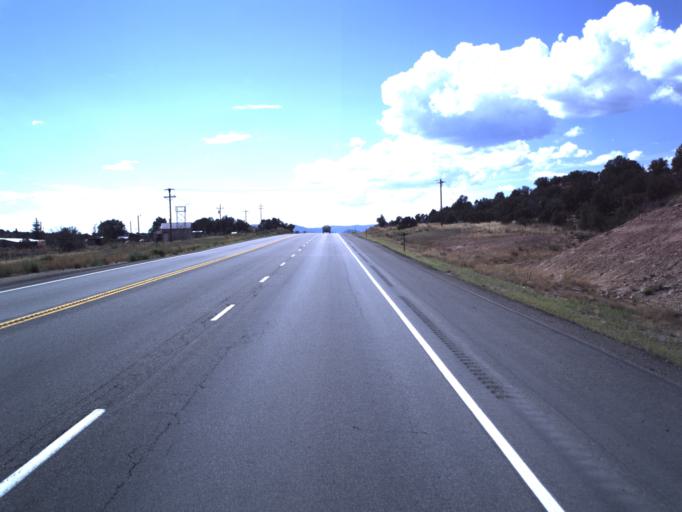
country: US
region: Utah
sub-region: Duchesne County
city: Duchesne
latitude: 40.2035
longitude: -110.7933
